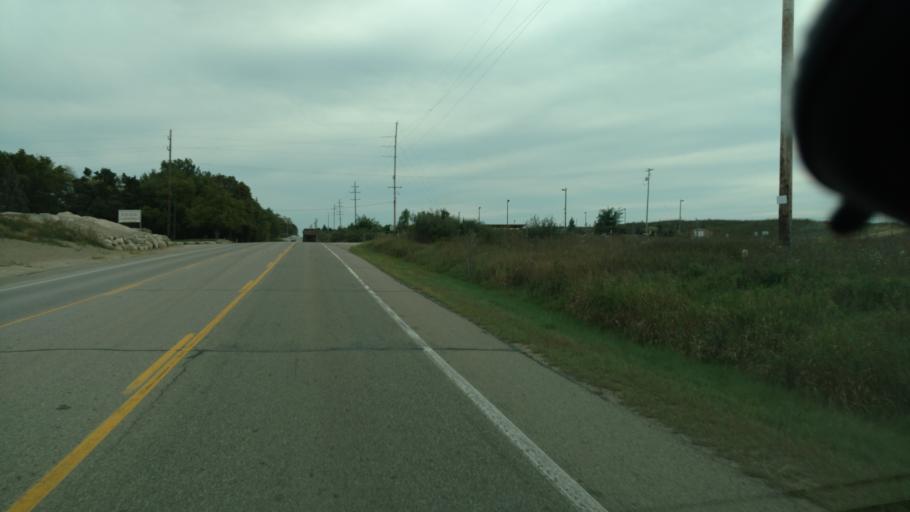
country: US
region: Michigan
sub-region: Ingham County
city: Lansing
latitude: 42.7780
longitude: -84.5232
